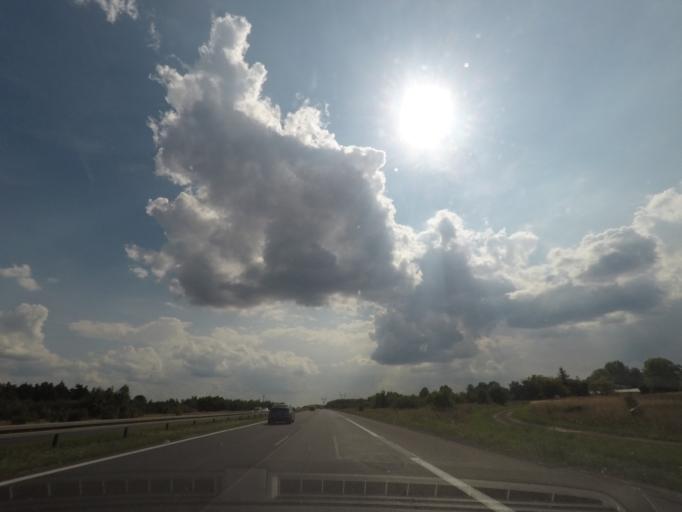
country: PL
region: Lodz Voivodeship
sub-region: Powiat piotrkowski
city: Wola Krzysztoporska
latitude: 51.2981
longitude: 19.5499
